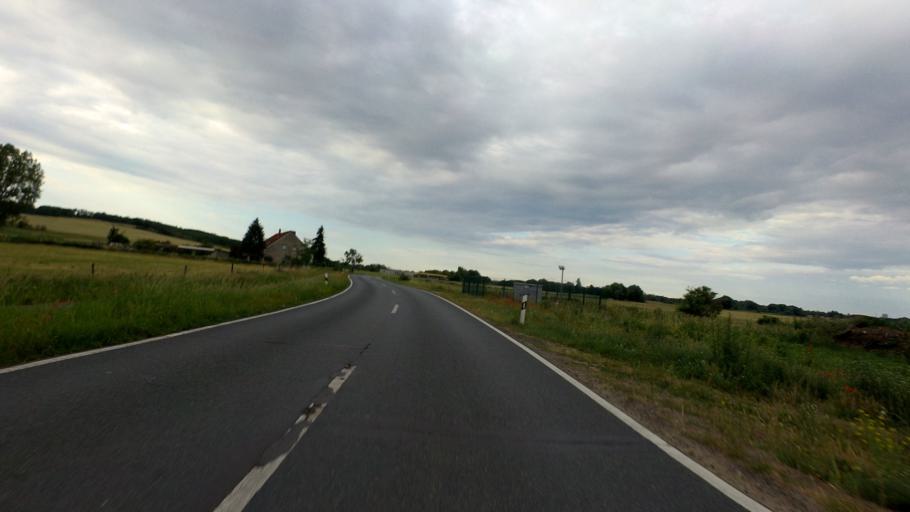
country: DE
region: Brandenburg
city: Ketzin
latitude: 52.4845
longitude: 12.7900
